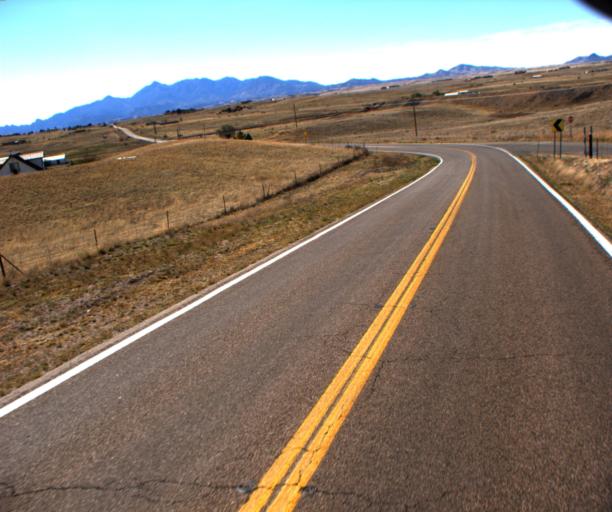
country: US
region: Arizona
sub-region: Cochise County
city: Huachuca City
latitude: 31.6731
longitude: -110.6108
